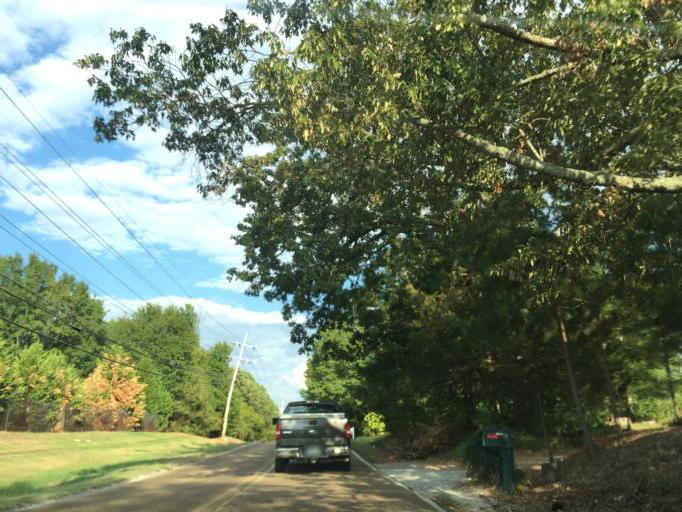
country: US
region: Mississippi
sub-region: Madison County
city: Madison
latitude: 32.4650
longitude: -90.0982
